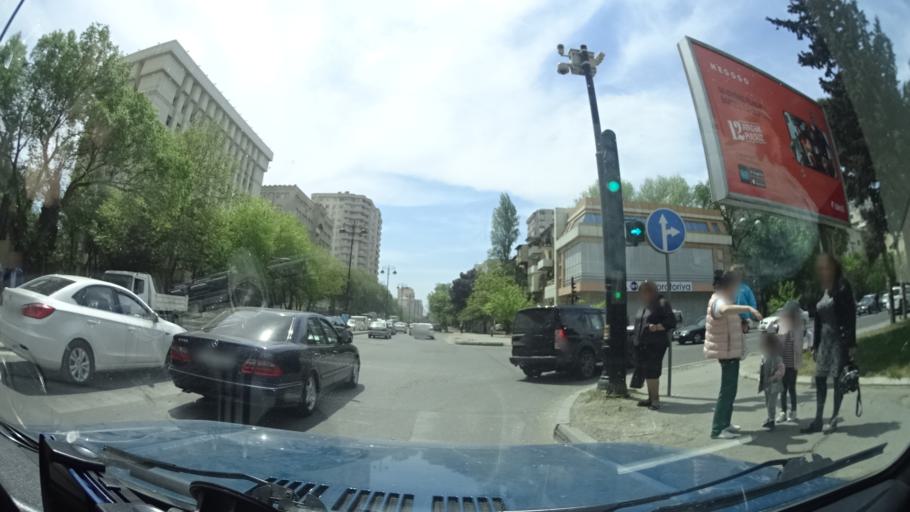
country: AZ
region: Baki
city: Khodzhi-Gasan
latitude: 40.3950
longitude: 49.8062
